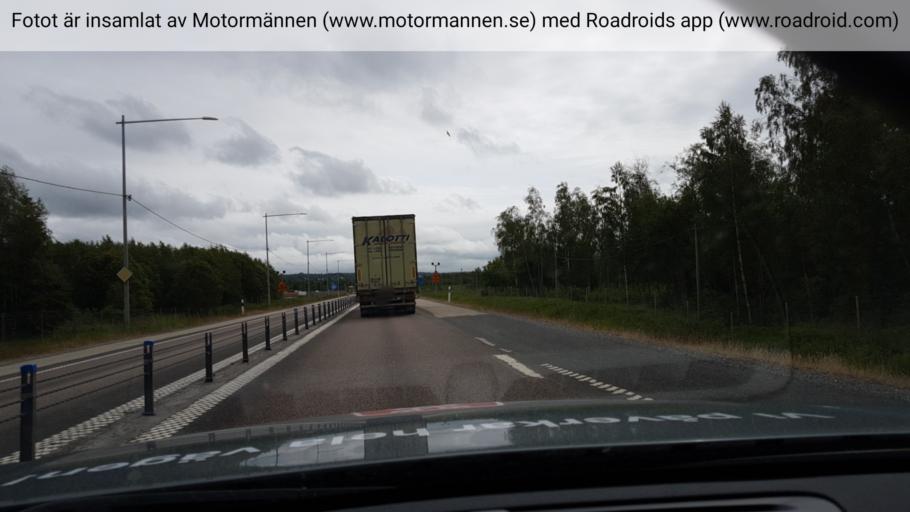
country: SE
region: Vaesternorrland
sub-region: Timra Kommun
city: Bergeforsen
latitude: 62.5176
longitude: 17.4432
